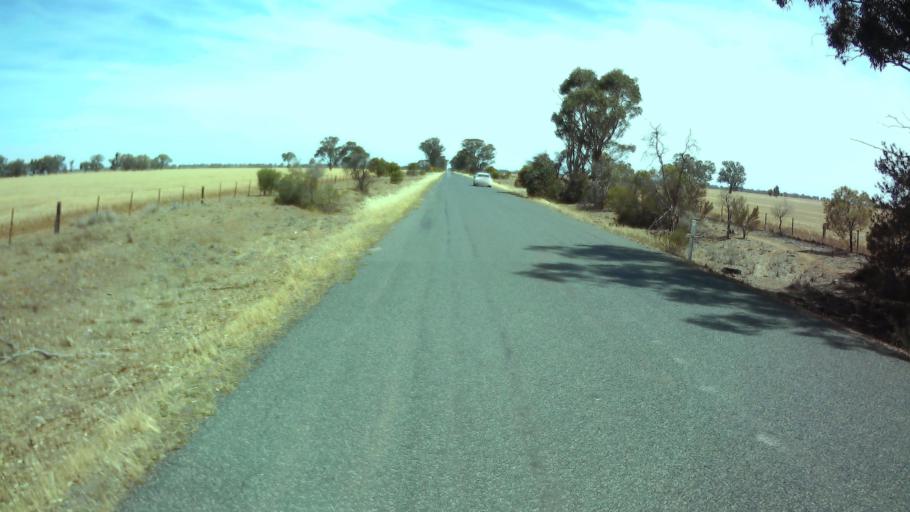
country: AU
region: New South Wales
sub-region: Weddin
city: Grenfell
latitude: -33.9653
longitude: 147.7810
